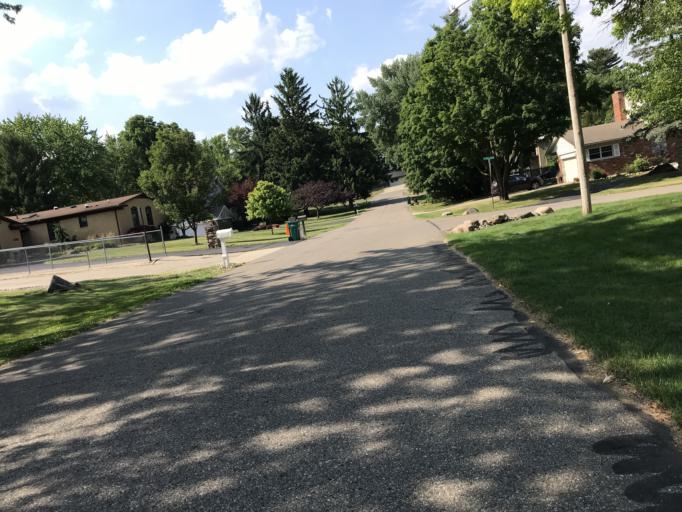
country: US
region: Michigan
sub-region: Oakland County
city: Farmington
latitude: 42.4655
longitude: -83.3904
